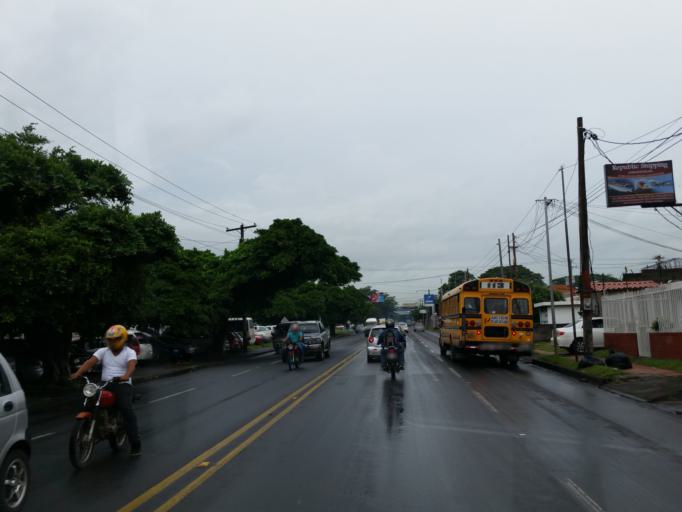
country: NI
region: Managua
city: Managua
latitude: 12.1439
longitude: -86.2922
